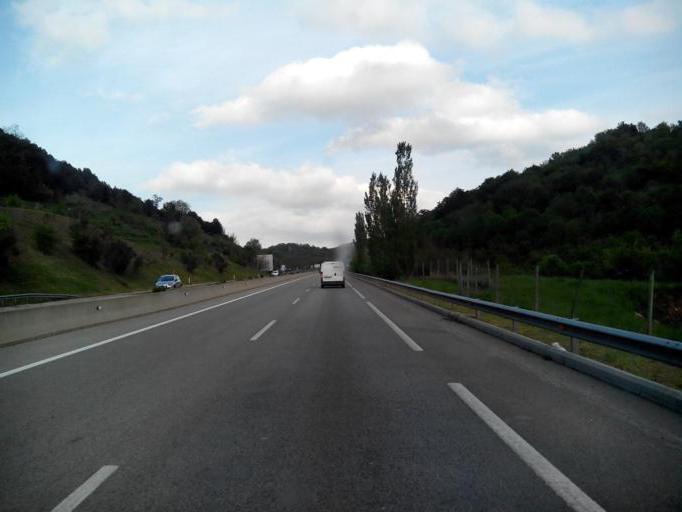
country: ES
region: Catalonia
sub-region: Provincia de Girona
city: Sant Joan les Fonts
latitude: 42.1934
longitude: 2.5125
